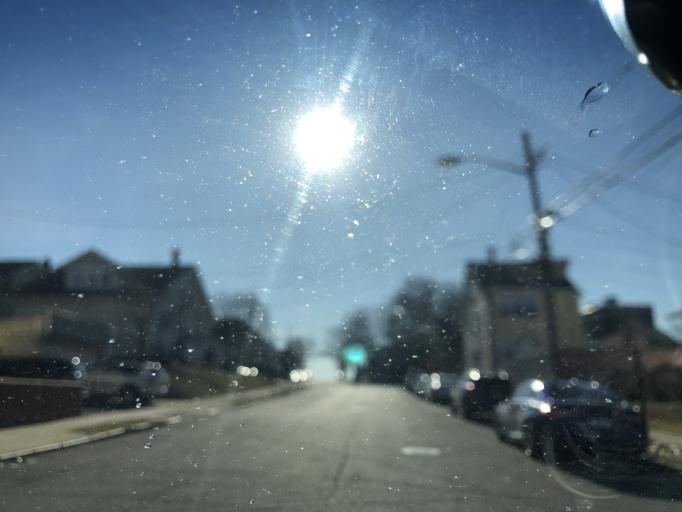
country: US
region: New Jersey
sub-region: Bergen County
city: Fair Lawn
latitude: 40.9220
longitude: -74.1459
